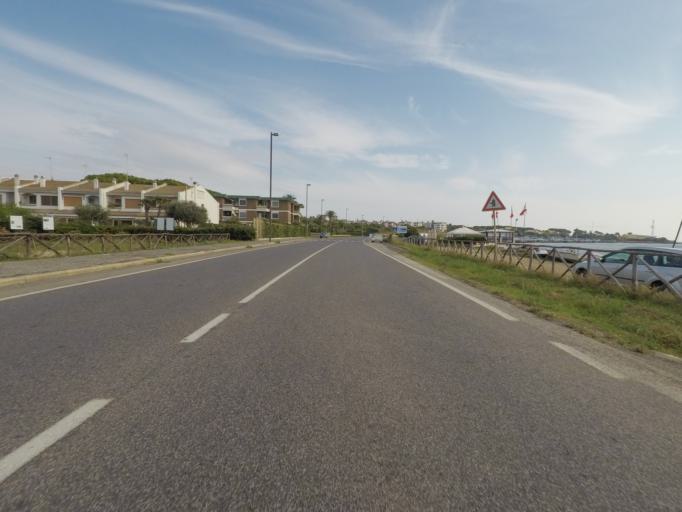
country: IT
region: Latium
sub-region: Citta metropolitana di Roma Capitale
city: Santa Marinella
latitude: 42.0390
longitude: 11.8310
